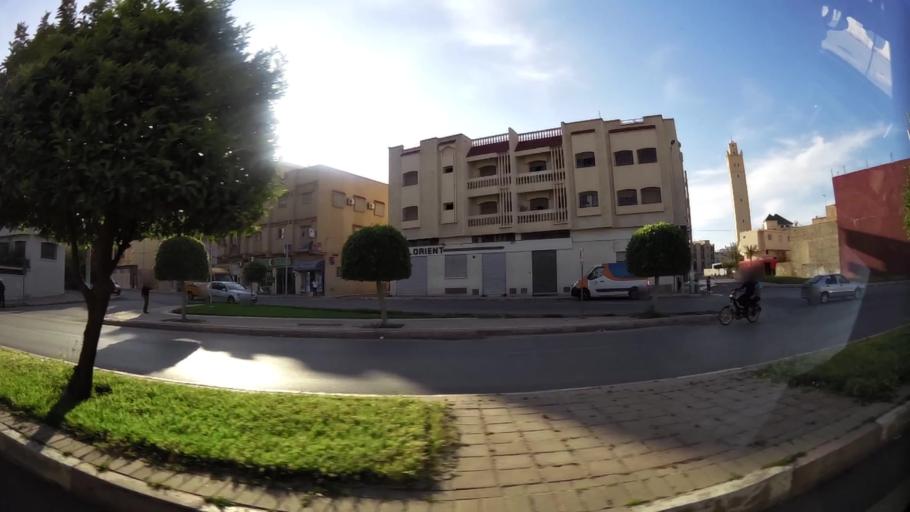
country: MA
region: Oriental
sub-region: Oujda-Angad
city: Oujda
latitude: 34.6994
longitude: -1.8989
